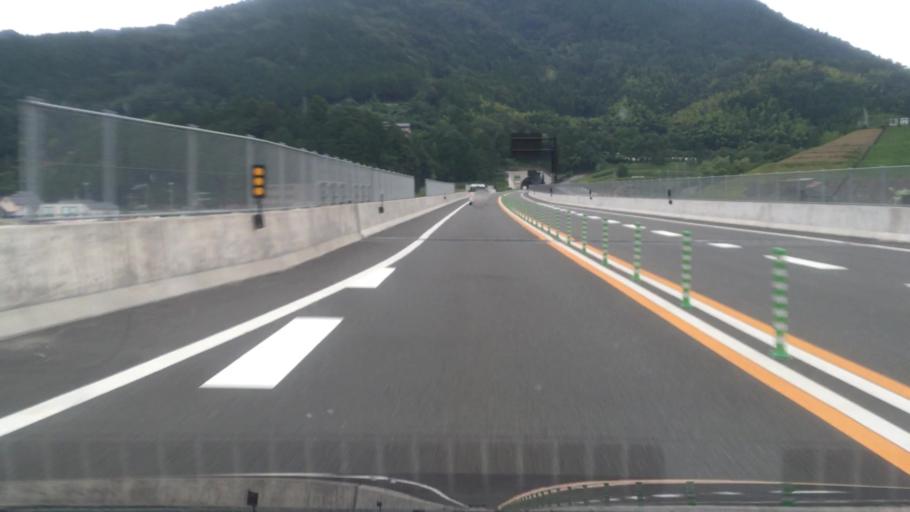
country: JP
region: Hyogo
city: Toyooka
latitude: 35.3926
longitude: 134.7459
